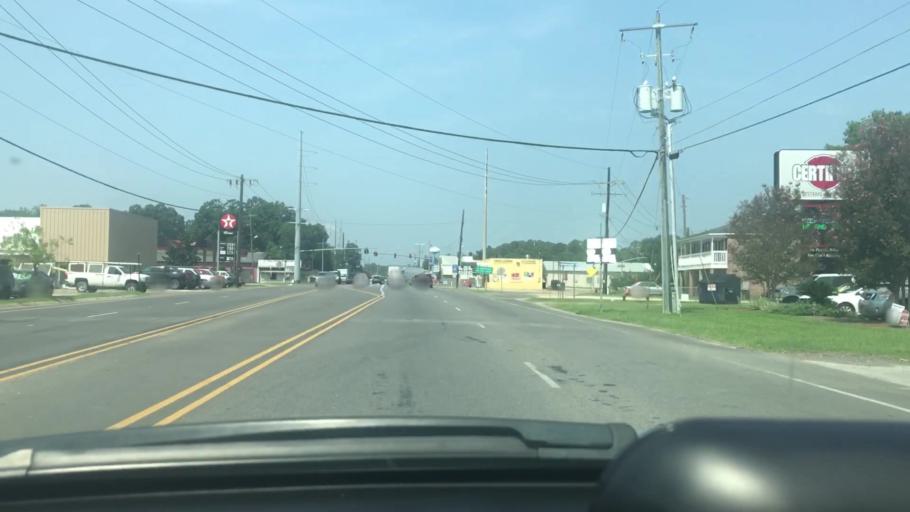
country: US
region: Louisiana
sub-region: Livingston Parish
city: Denham Springs
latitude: 30.4843
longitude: -90.9418
